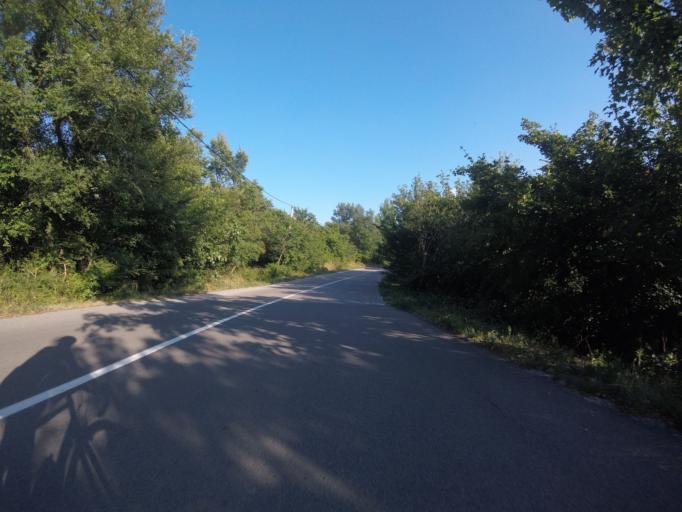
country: HR
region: Primorsko-Goranska
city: Selce
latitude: 45.1777
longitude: 14.7405
